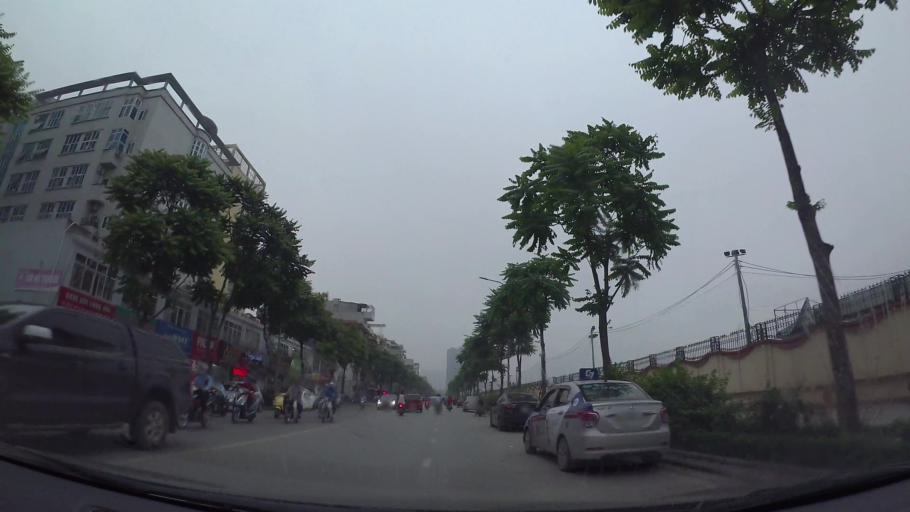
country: VN
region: Ha Noi
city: Hai BaTrung
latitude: 20.9927
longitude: 105.8323
